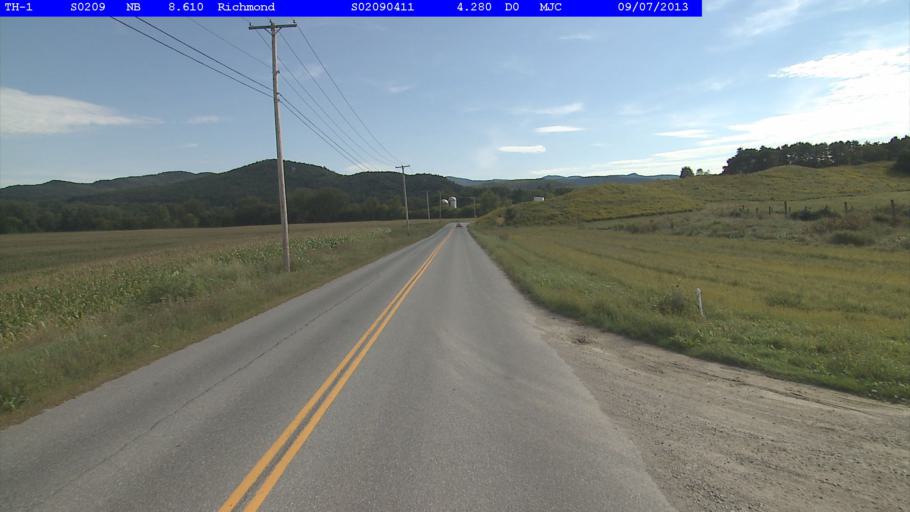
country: US
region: Vermont
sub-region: Chittenden County
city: Williston
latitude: 44.3986
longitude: -73.0069
